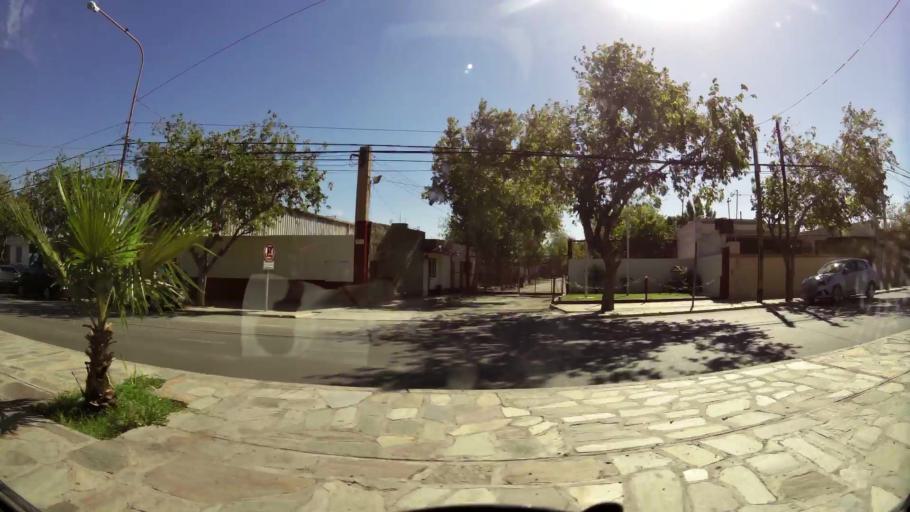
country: AR
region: San Juan
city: San Juan
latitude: -31.5491
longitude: -68.5331
